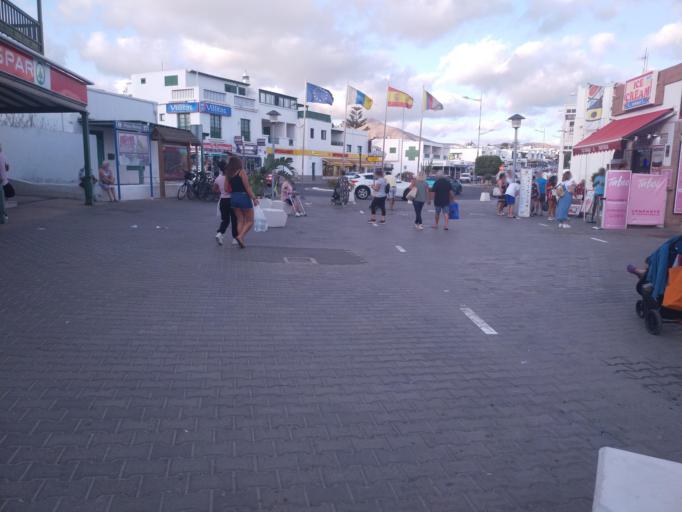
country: ES
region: Canary Islands
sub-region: Provincia de Las Palmas
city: Playa Blanca
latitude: 28.8630
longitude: -13.8302
